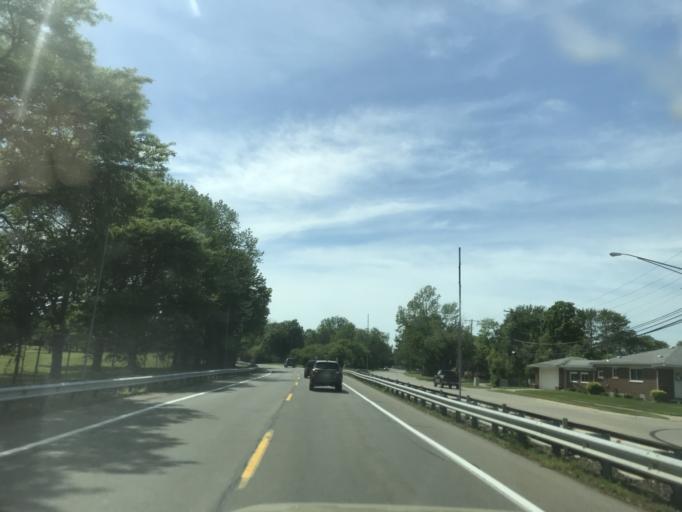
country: US
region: Michigan
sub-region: Wayne County
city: Dearborn Heights
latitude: 42.3519
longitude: -83.2965
